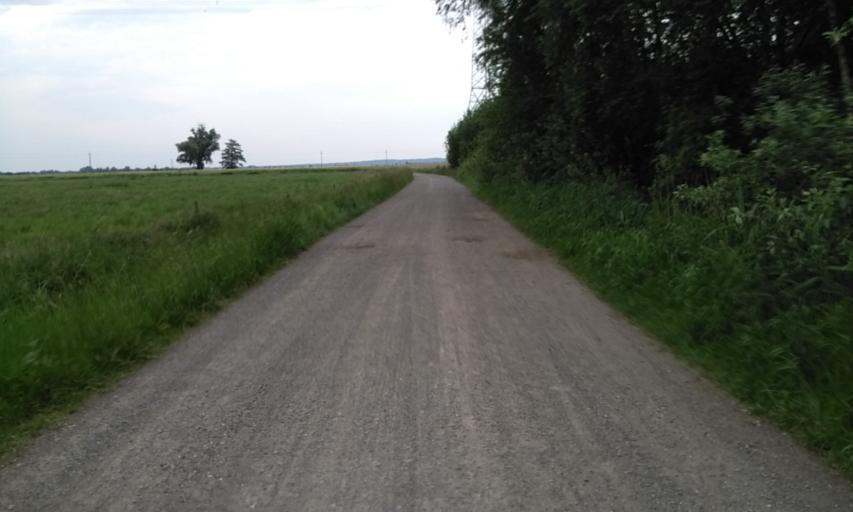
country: DE
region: Lower Saxony
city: Buxtehude
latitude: 53.4922
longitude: 9.6851
